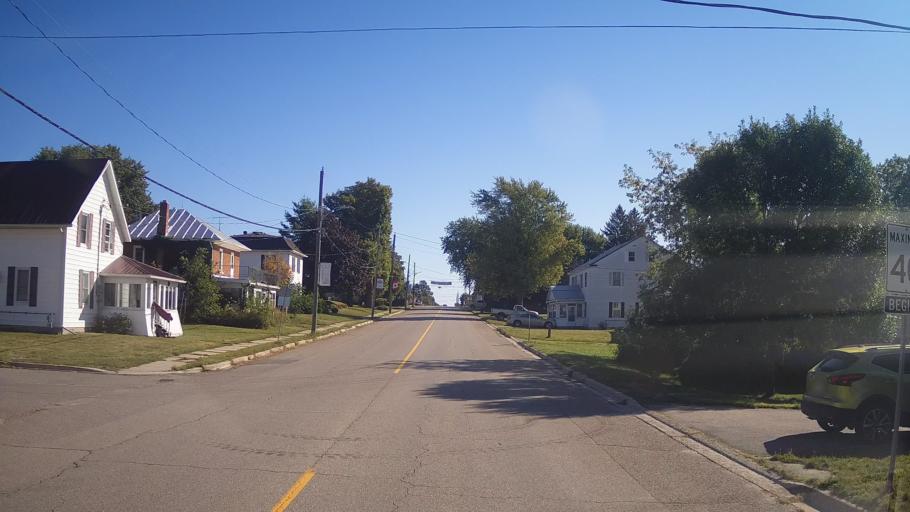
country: CA
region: Ontario
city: Brockville
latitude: 44.6249
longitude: -75.9549
